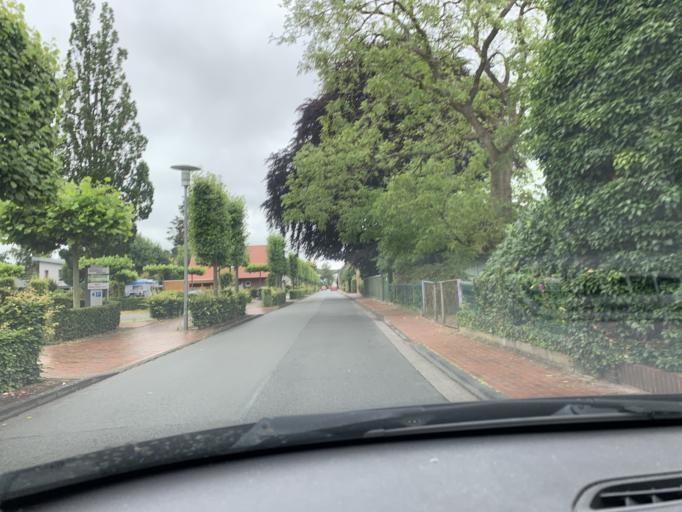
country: DE
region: Lower Saxony
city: Westerstede
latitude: 53.2575
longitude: 7.9224
